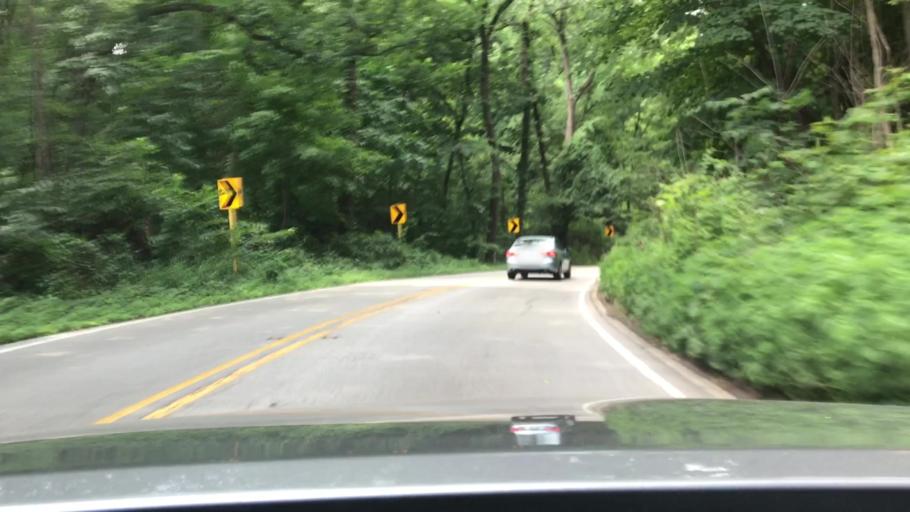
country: US
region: Illinois
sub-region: DuPage County
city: Burr Ridge
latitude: 41.7149
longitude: -87.8955
